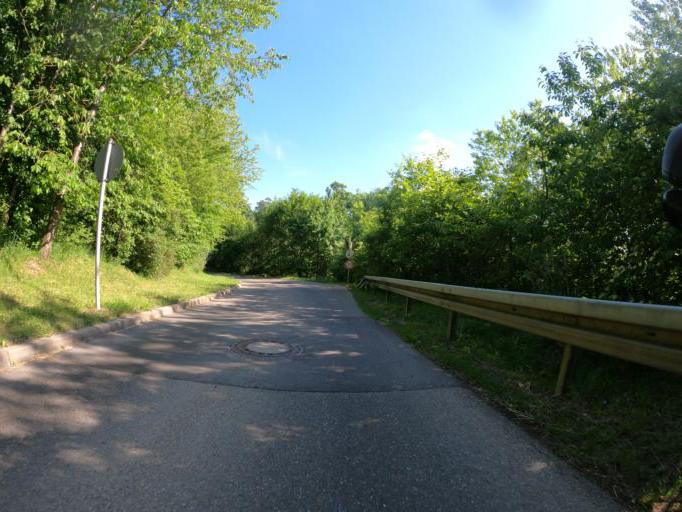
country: DE
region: Baden-Wuerttemberg
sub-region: Regierungsbezirk Stuttgart
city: Leonberg
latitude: 48.7540
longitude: 9.0347
